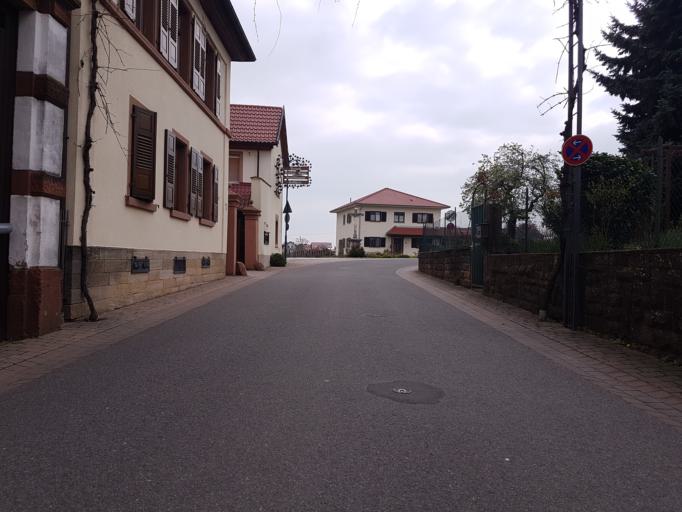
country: DE
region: Rheinland-Pfalz
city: Flemlingen
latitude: 49.2430
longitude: 8.0955
